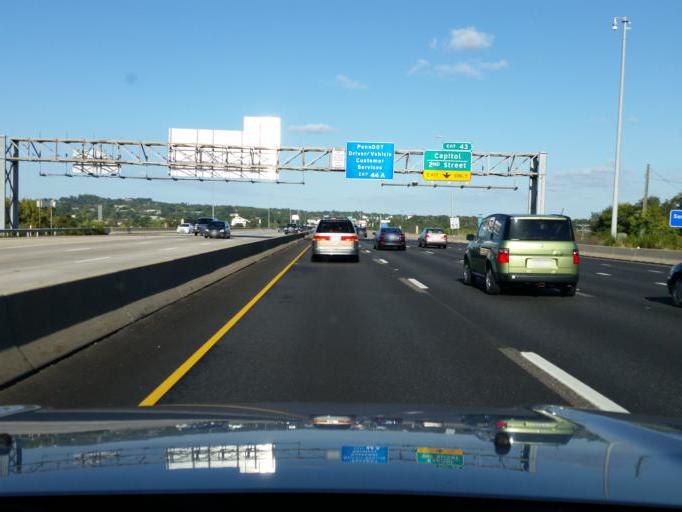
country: US
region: Pennsylvania
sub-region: Cumberland County
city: Lemoyne
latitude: 40.2448
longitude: -76.8839
